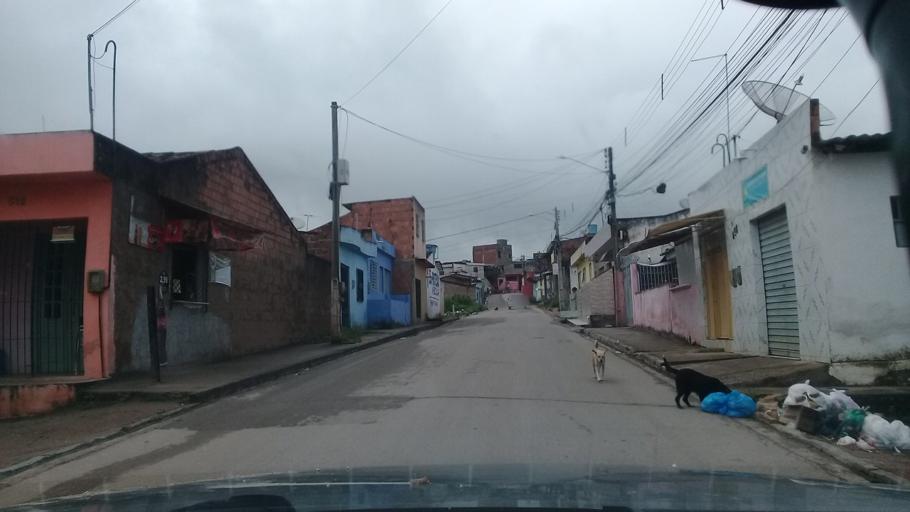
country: BR
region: Pernambuco
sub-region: Vitoria De Santo Antao
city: Vitoria de Santo Antao
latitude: -8.1281
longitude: -35.2879
